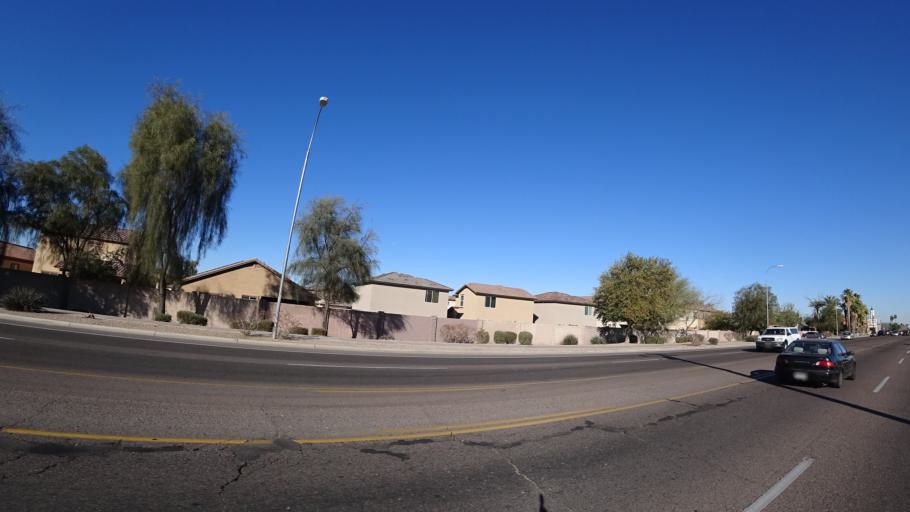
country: US
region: Arizona
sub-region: Maricopa County
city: Phoenix
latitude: 33.3921
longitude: -112.0858
